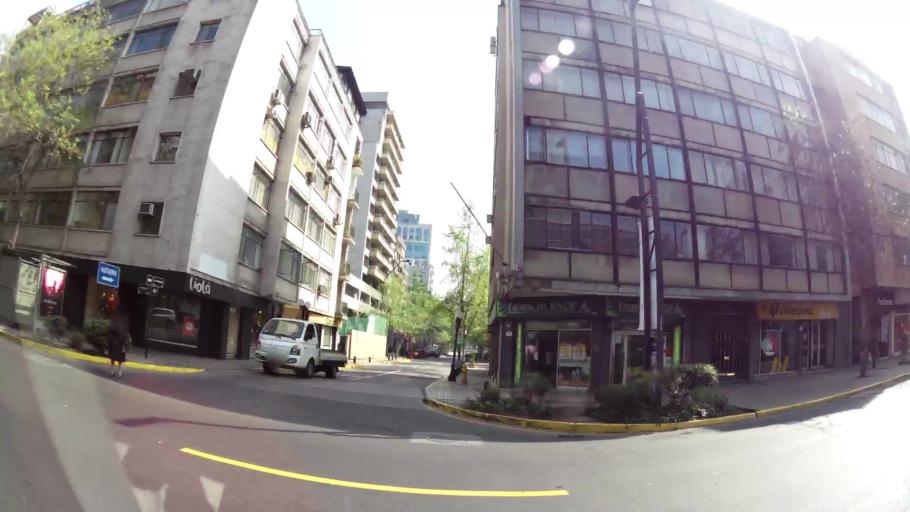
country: CL
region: Santiago Metropolitan
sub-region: Provincia de Santiago
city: Villa Presidente Frei, Nunoa, Santiago, Chile
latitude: -33.4214
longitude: -70.6091
